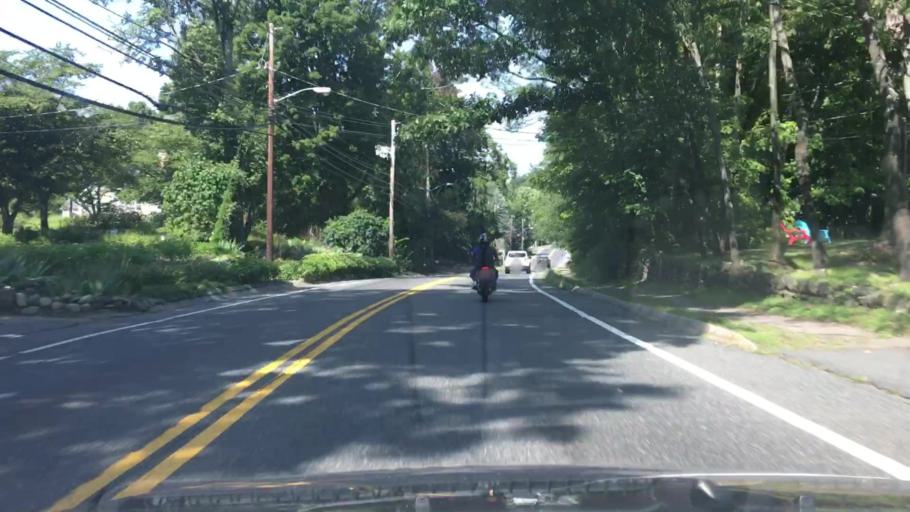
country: US
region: Massachusetts
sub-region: Middlesex County
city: Holliston
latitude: 42.1928
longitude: -71.4361
